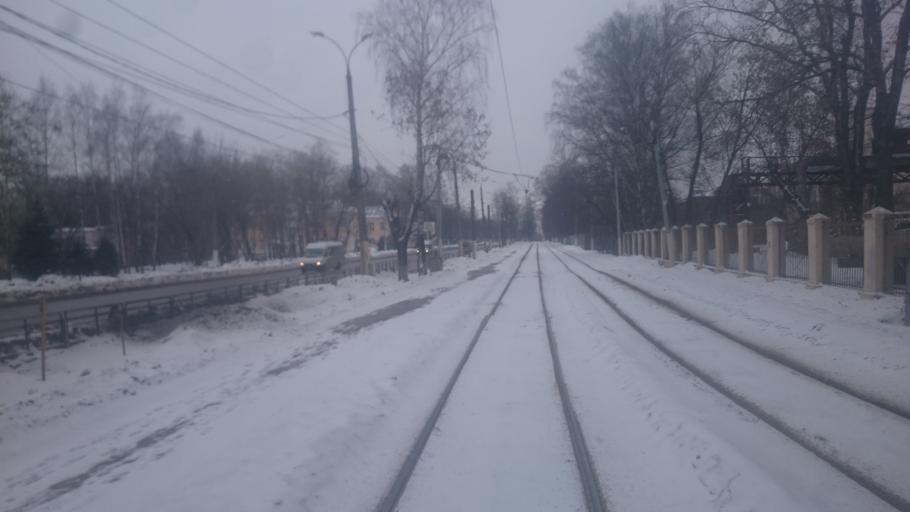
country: RU
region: Tverskaya
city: Tver
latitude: 56.8699
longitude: 35.8774
